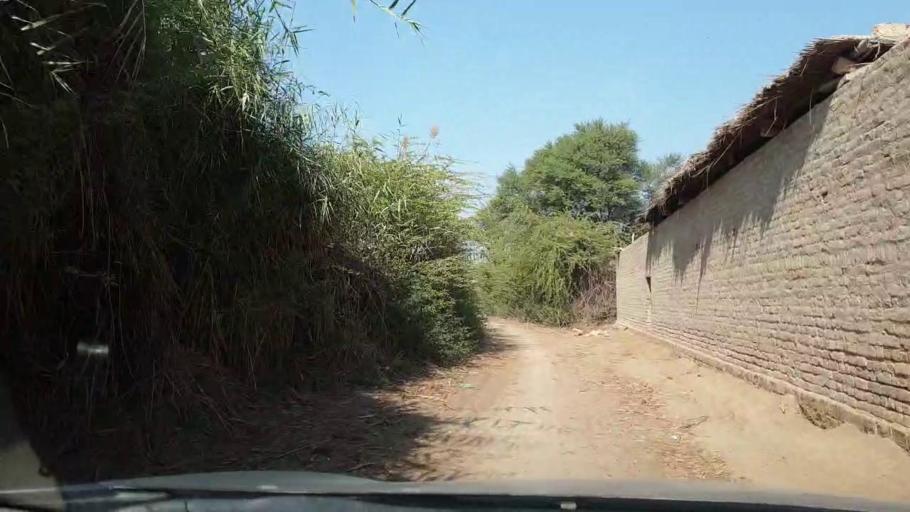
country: PK
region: Sindh
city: Berani
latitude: 25.6882
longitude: 68.7519
